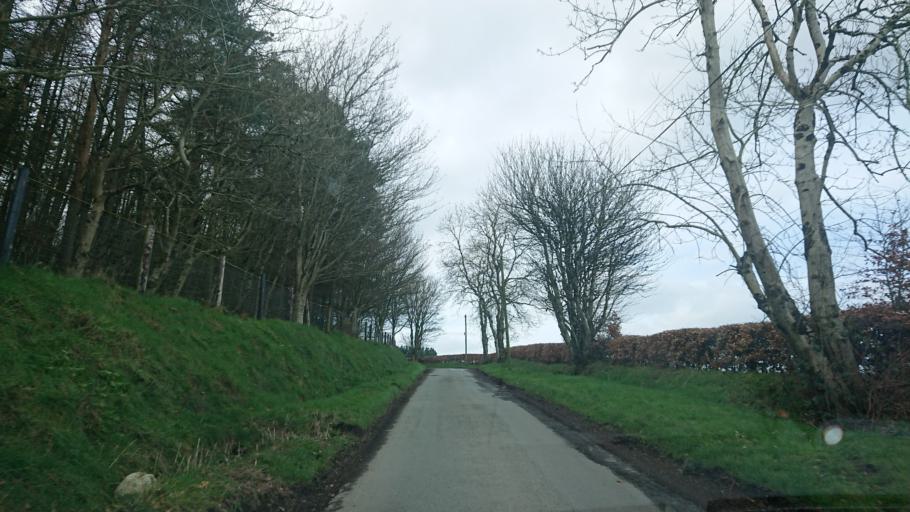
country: IE
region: Leinster
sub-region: Wicklow
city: Blessington
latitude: 53.1561
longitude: -6.5704
